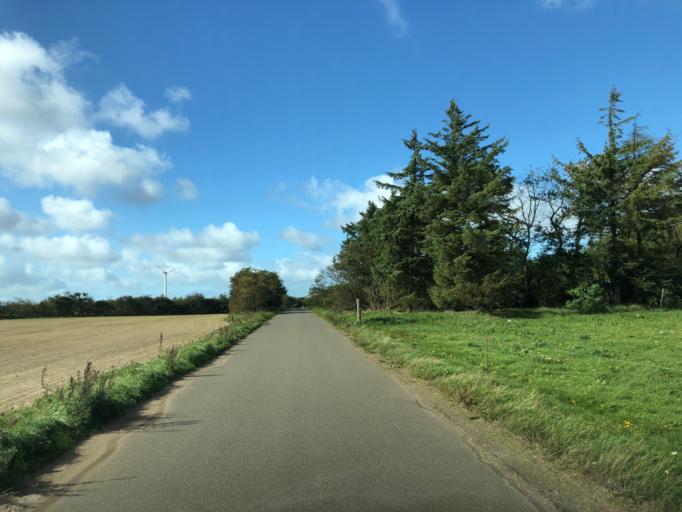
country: DK
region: Central Jutland
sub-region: Holstebro Kommune
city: Ulfborg
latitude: 56.2910
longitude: 8.3236
